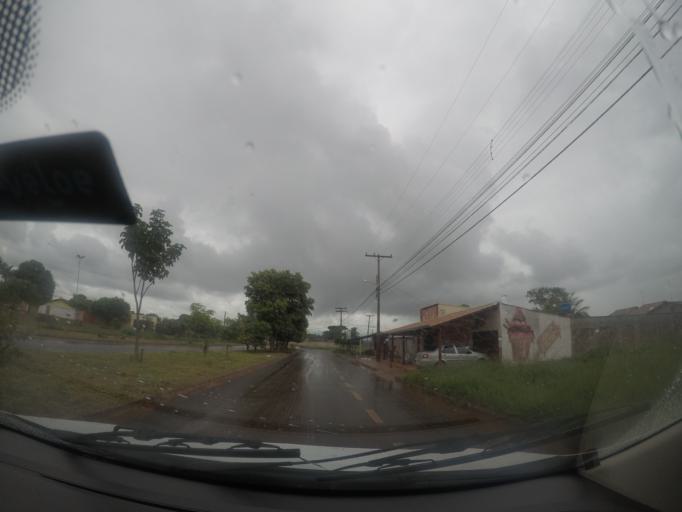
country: BR
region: Goias
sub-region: Trindade
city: Trindade
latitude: -16.6409
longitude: -49.4393
